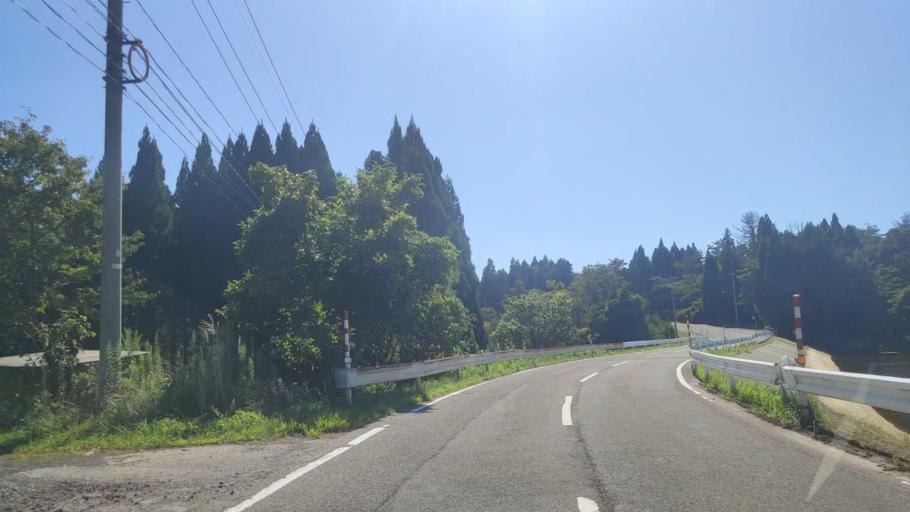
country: JP
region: Ishikawa
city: Nanao
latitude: 37.4747
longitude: 137.3340
